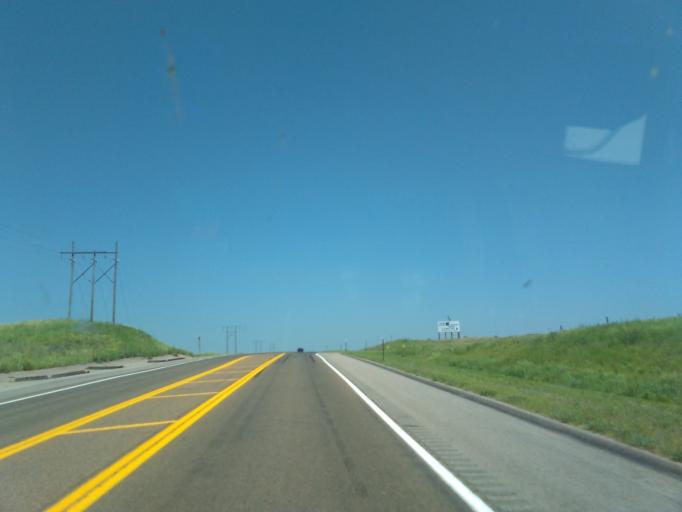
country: US
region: Nebraska
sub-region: Lincoln County
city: North Platte
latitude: 40.8732
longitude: -100.7540
